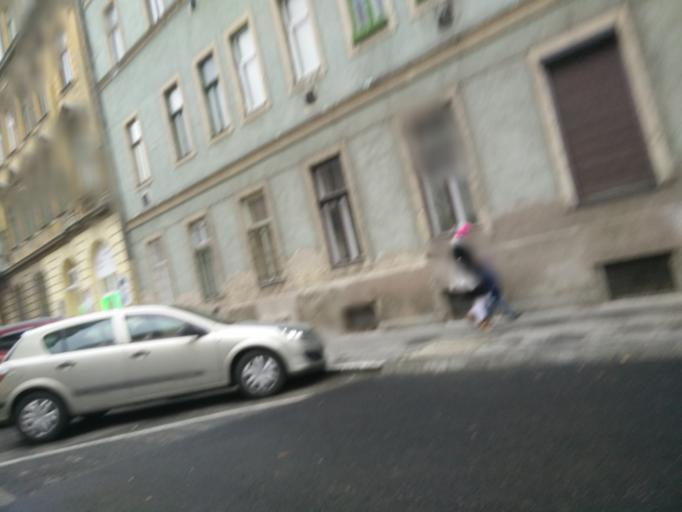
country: HU
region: Budapest
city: Budapest VIII. keruelet
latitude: 47.4947
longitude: 19.0814
